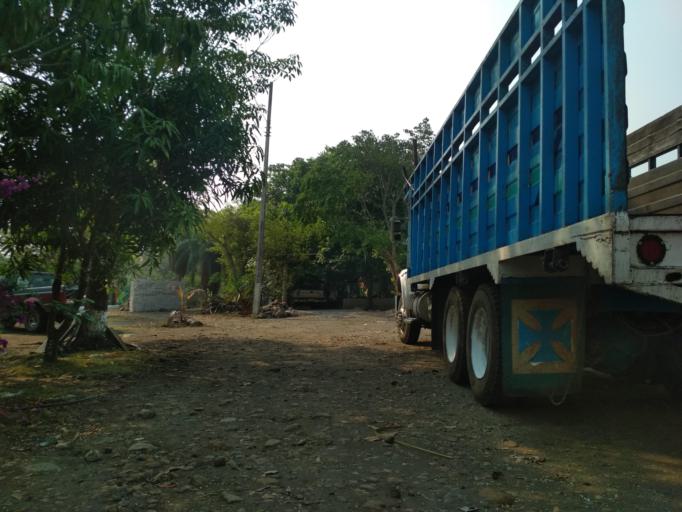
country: MX
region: Oaxaca
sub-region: Cosolapa
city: Cosolapa
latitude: 18.6246
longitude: -96.6033
